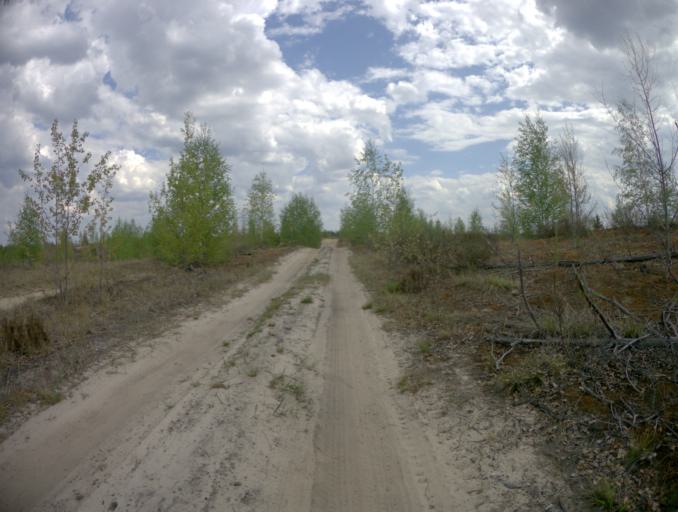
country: RU
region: Ivanovo
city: Talitsy
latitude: 56.4629
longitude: 42.2224
